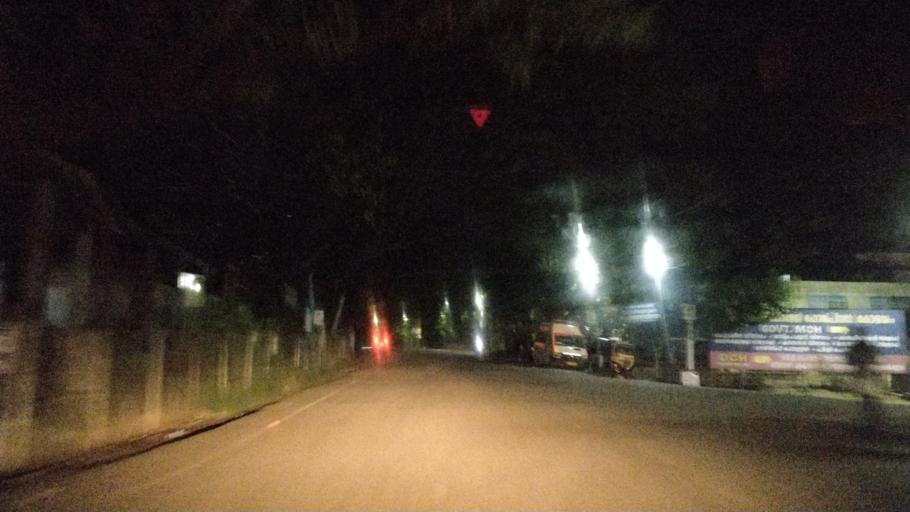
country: IN
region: Kerala
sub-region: Kottayam
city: Kottayam
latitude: 9.6326
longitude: 76.5216
